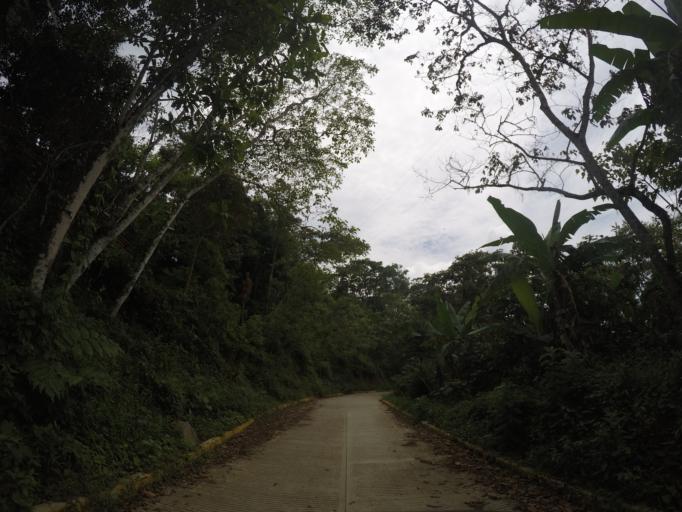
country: MX
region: Oaxaca
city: Pluma Hidalgo
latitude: 15.9171
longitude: -96.4157
